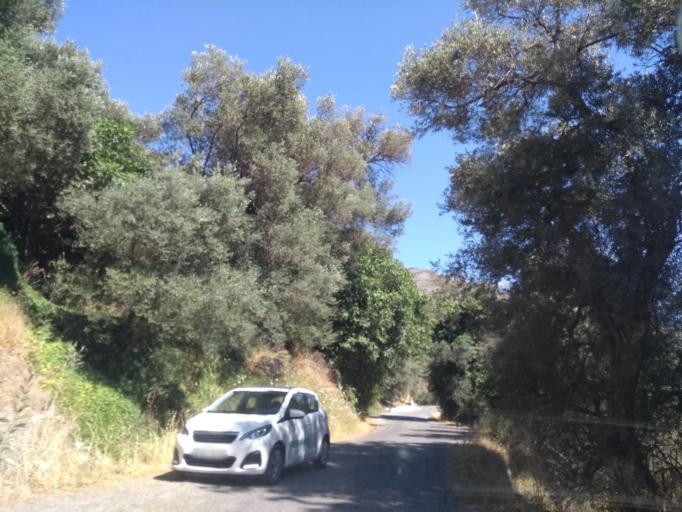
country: GR
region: Crete
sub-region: Nomos Chanias
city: Vryses
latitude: 35.3643
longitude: 23.5929
